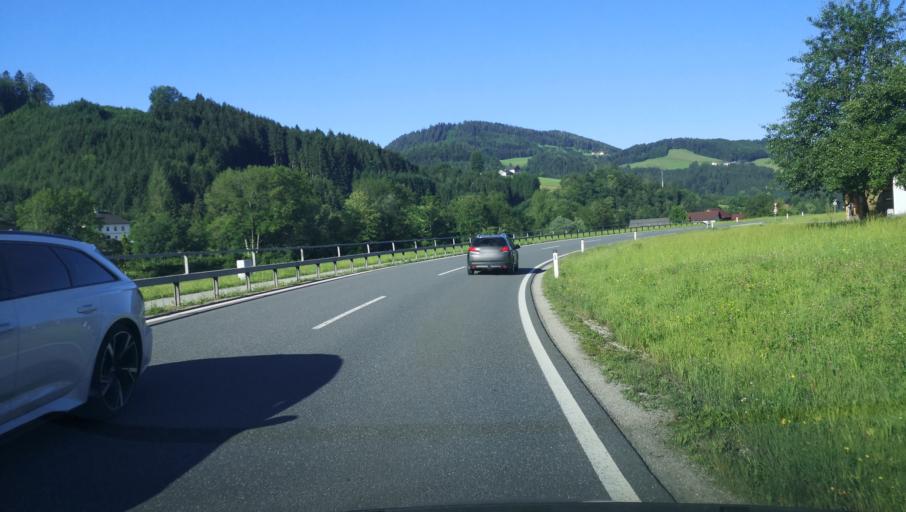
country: AT
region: Lower Austria
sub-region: Politischer Bezirk Amstetten
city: Ybbsitz
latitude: 47.9426
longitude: 14.8679
